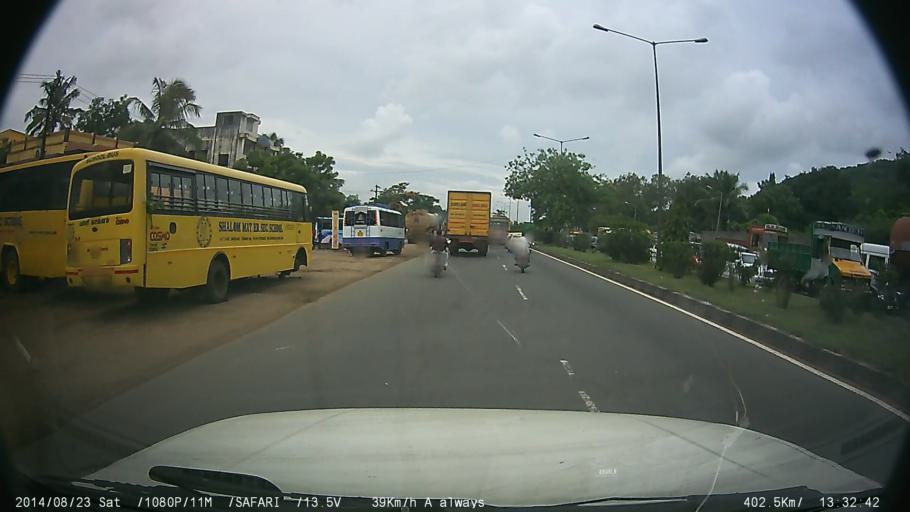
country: IN
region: Tamil Nadu
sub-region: Kancheepuram
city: Vandalur
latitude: 12.8879
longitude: 80.0836
